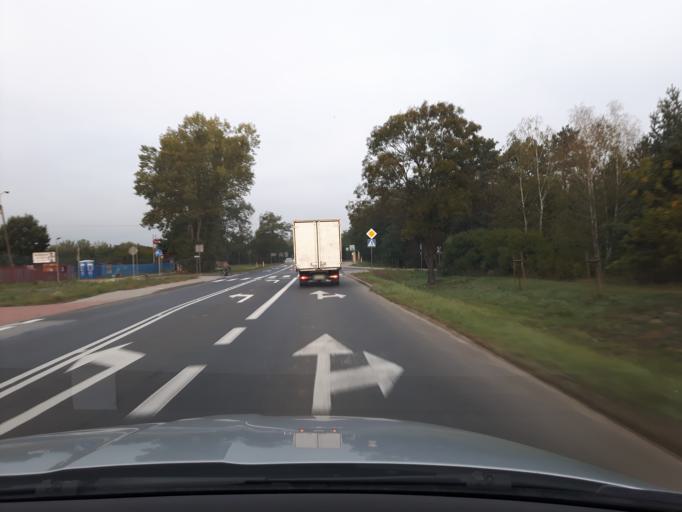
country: PL
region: Masovian Voivodeship
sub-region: Powiat warszawski zachodni
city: Dziekanow Lesny
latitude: 52.4074
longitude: 20.7943
